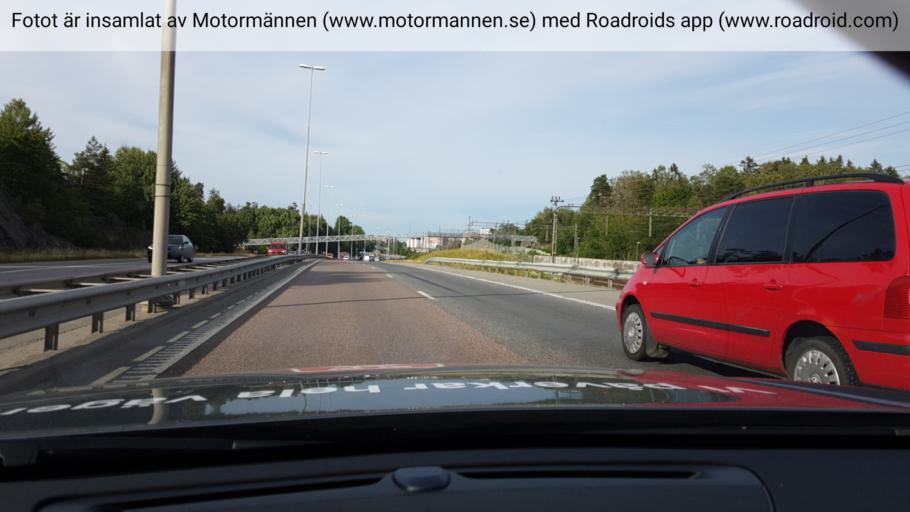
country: SE
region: Stockholm
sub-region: Huddinge Kommun
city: Huddinge
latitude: 59.2298
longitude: 17.9652
